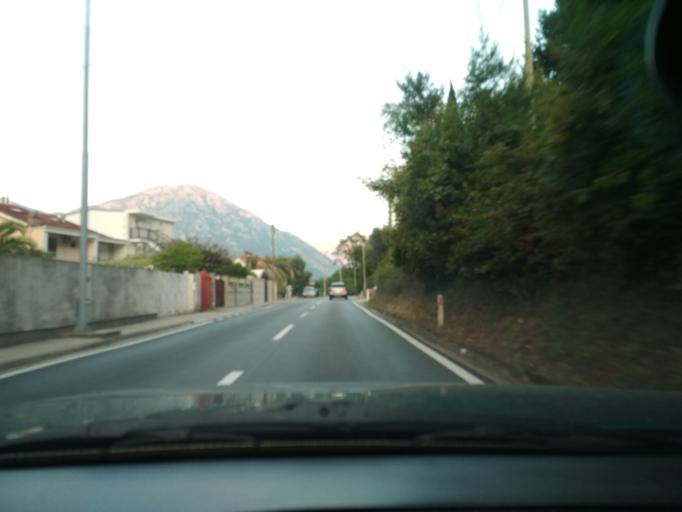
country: ME
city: Lipci
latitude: 42.4871
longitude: 18.6534
